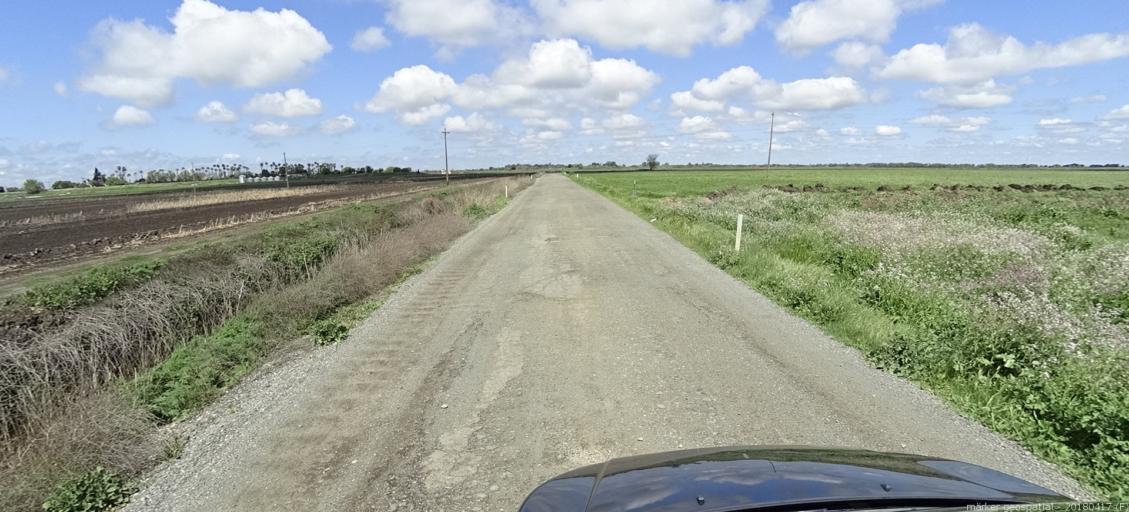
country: US
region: California
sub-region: Solano County
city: Rio Vista
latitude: 38.1428
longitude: -121.5824
